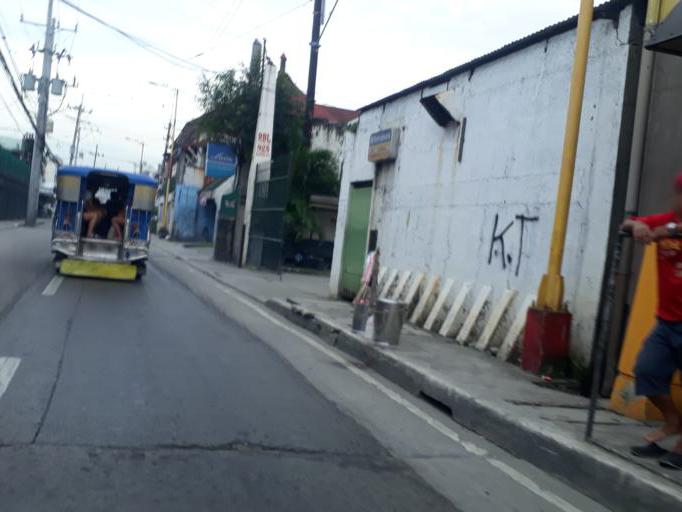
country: PH
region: Calabarzon
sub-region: Province of Rizal
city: Navotas
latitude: 14.6598
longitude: 120.9467
